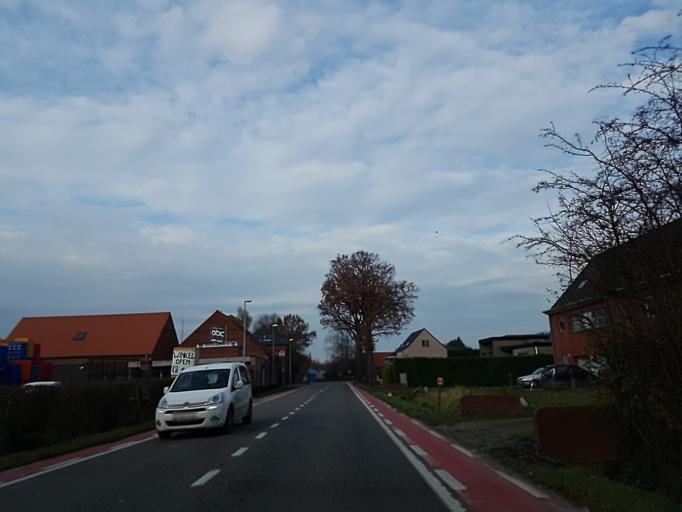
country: BE
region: Flanders
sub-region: Provincie Antwerpen
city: Kalmthout
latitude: 51.3980
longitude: 4.4727
